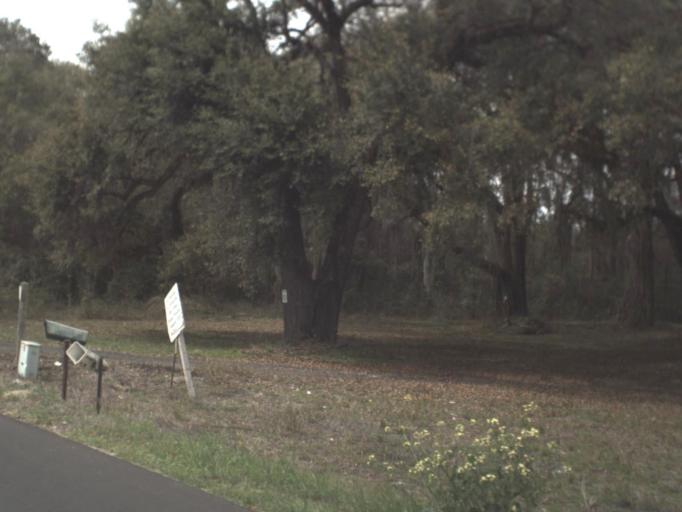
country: US
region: Florida
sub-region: Gadsden County
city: Midway
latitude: 30.4440
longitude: -84.3970
